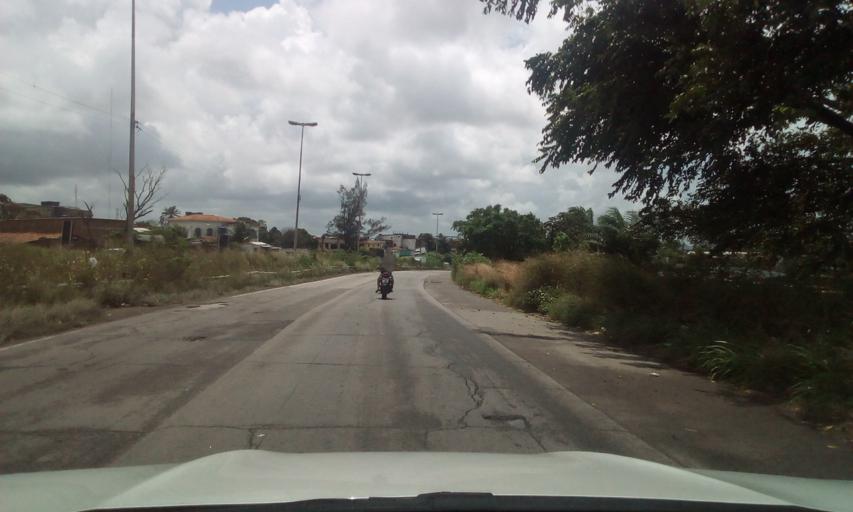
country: BR
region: Pernambuco
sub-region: Jaboatao Dos Guararapes
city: Jaboatao dos Guararapes
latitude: -8.0892
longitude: -34.9467
